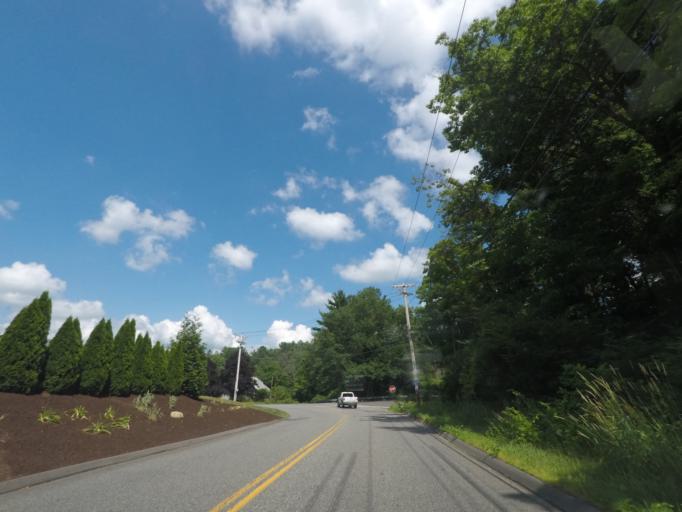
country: US
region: Massachusetts
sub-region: Hampden County
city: Monson
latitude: 42.1100
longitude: -72.3119
